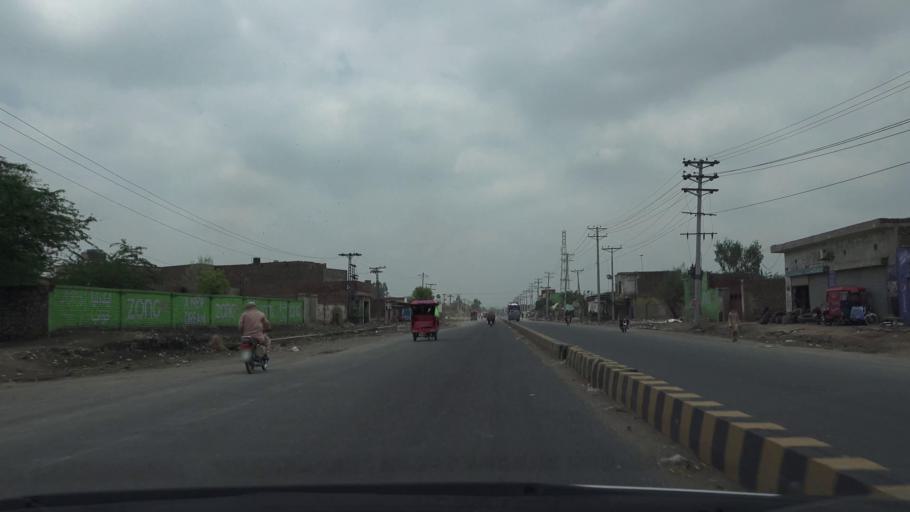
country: PK
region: Punjab
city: Faisalabad
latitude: 31.3928
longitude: 73.1827
